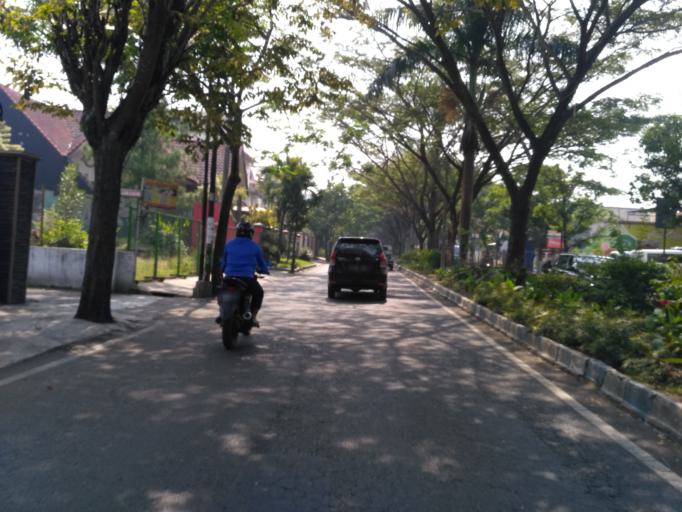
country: ID
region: East Java
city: Malang
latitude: -7.9766
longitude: 112.6610
